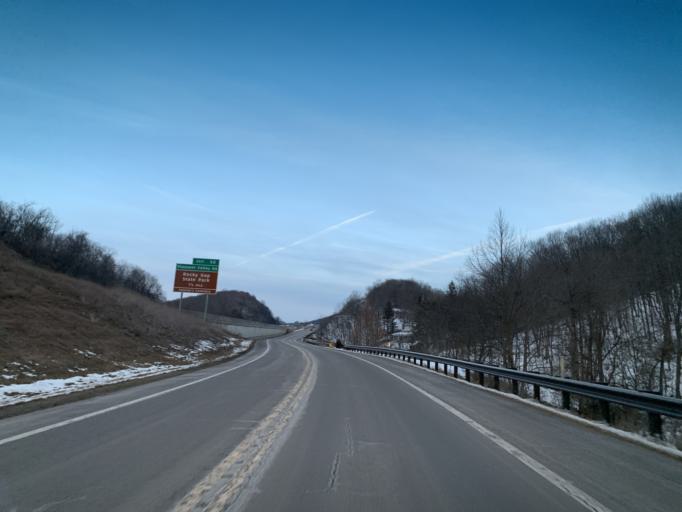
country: US
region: Maryland
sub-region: Allegany County
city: Cumberland
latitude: 39.6853
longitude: -78.6632
